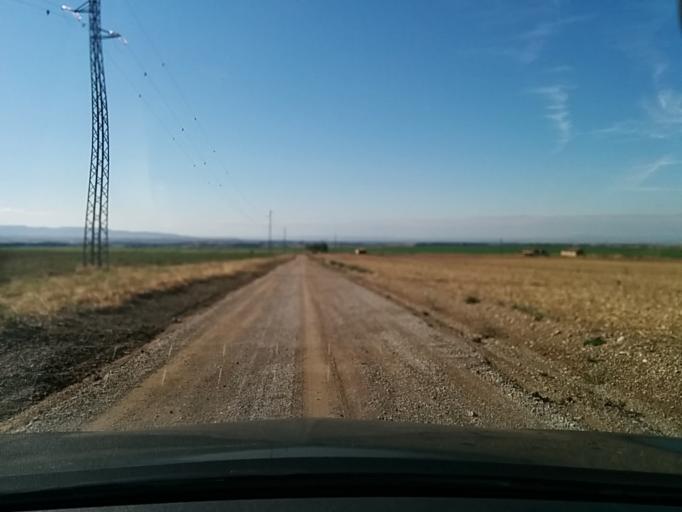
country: ES
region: Aragon
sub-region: Provincia de Zaragoza
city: Tauste
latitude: 42.0079
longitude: -1.3001
